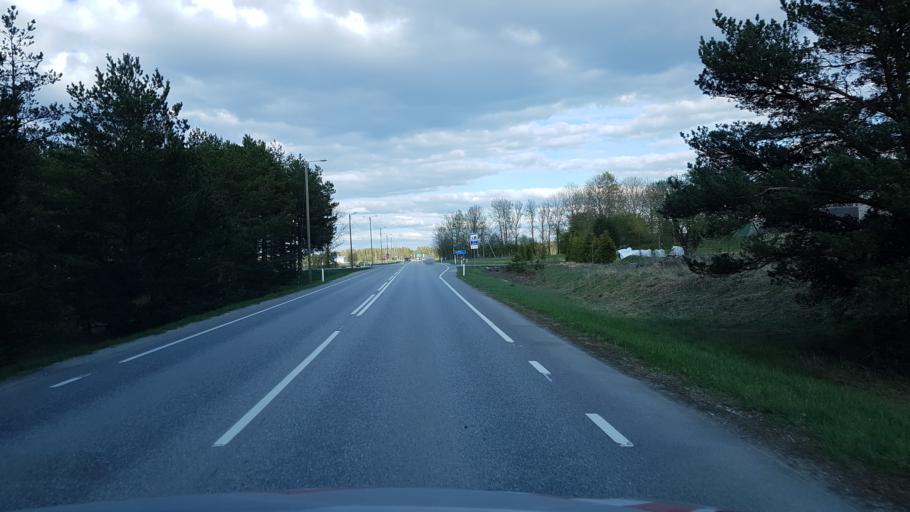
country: EE
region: Harju
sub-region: Saku vald
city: Saku
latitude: 59.2676
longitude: 24.7337
